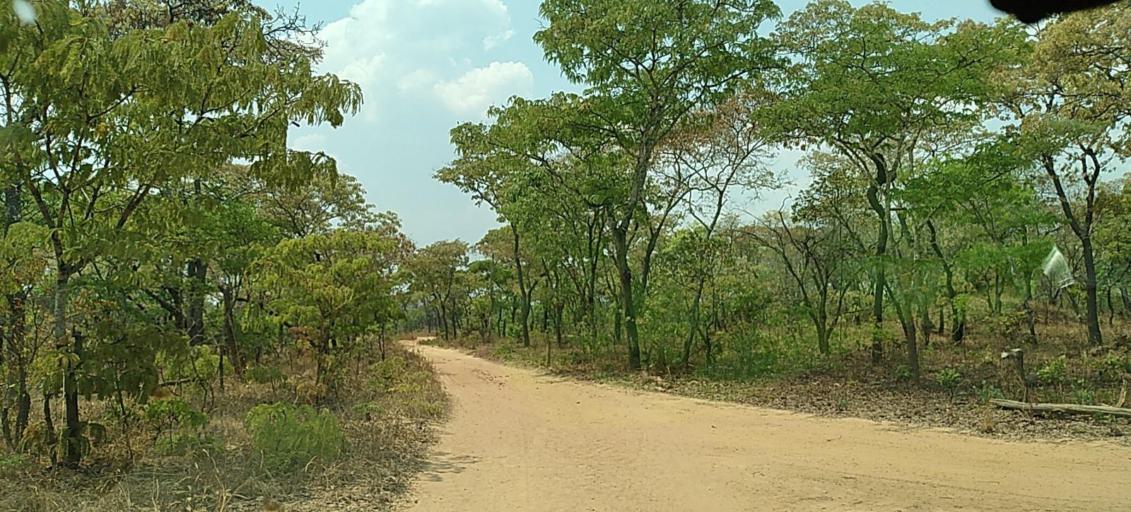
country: ZM
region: North-Western
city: Kabompo
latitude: -13.6381
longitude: 24.3842
